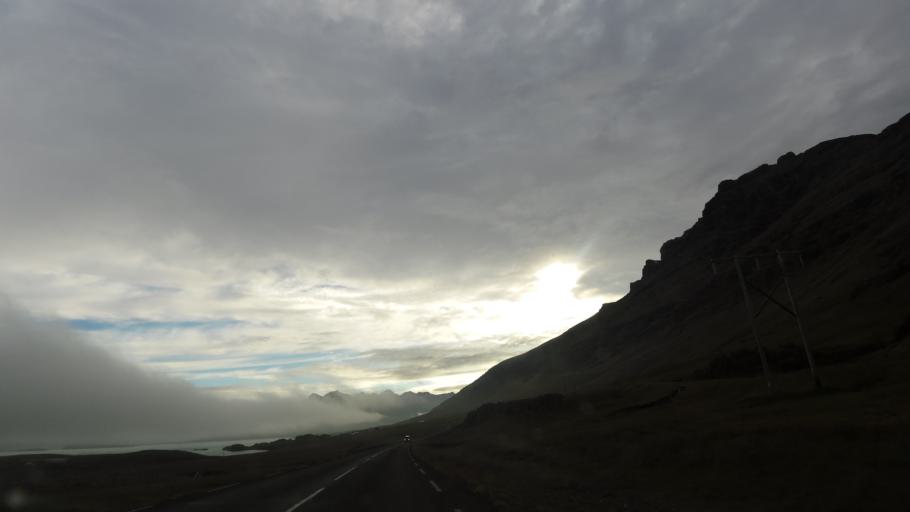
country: IS
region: East
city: Reydarfjoerdur
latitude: 64.5965
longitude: -14.4738
